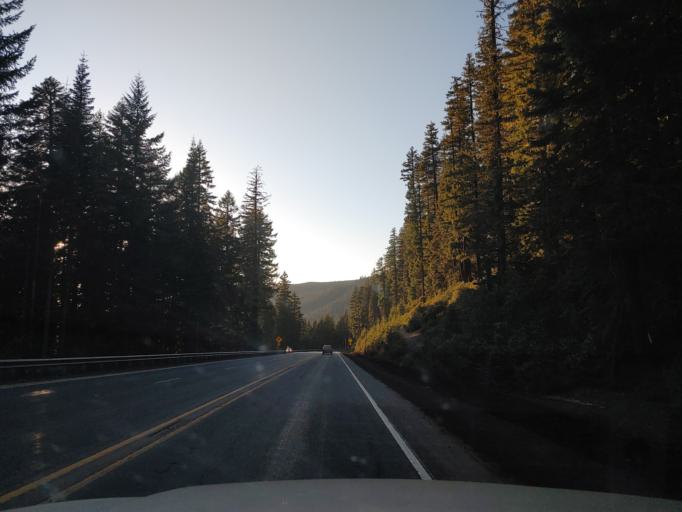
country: US
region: Oregon
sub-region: Lane County
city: Oakridge
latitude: 43.6124
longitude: -122.0655
